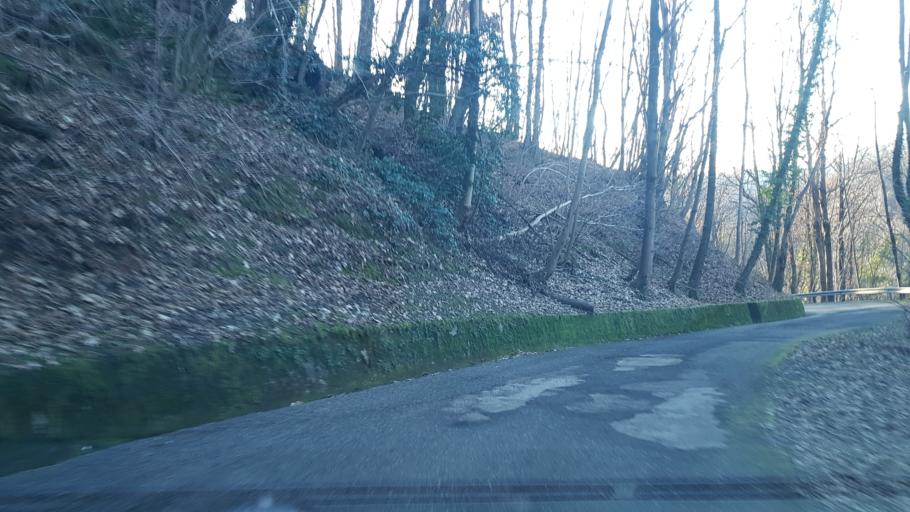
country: IT
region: Friuli Venezia Giulia
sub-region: Provincia di Udine
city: Tarcento
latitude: 46.2362
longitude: 13.2234
